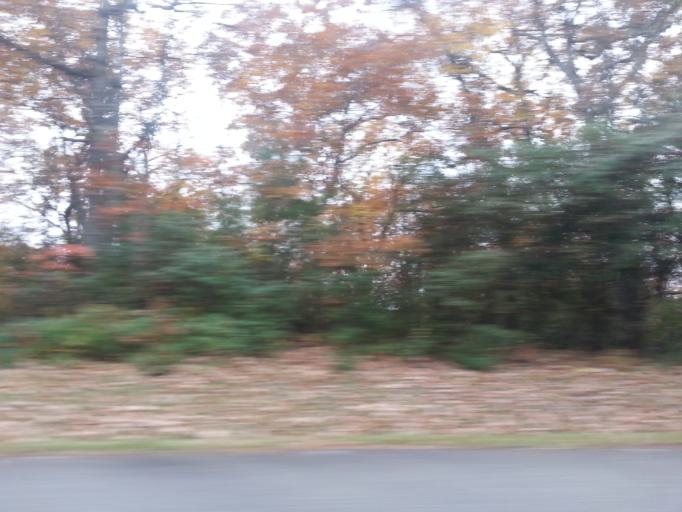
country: US
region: North Carolina
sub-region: Ashe County
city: West Jefferson
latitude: 36.2828
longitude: -81.3881
